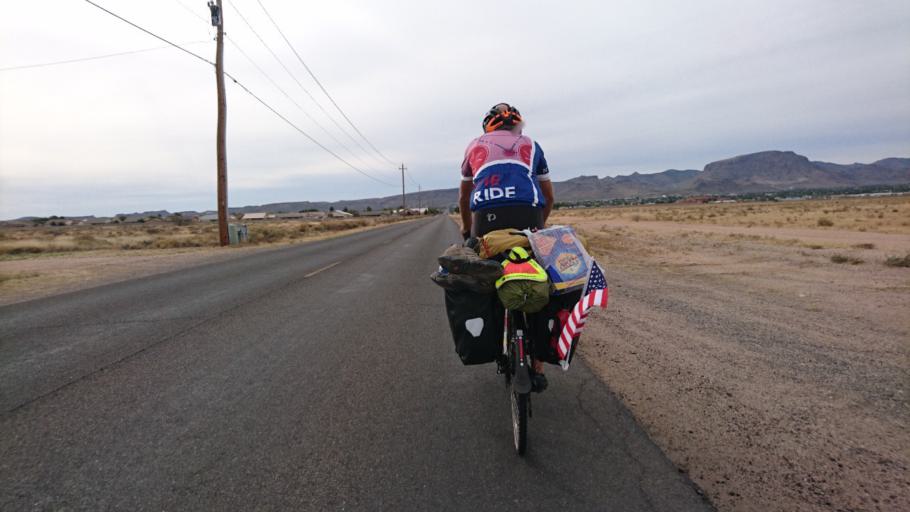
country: US
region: Arizona
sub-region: Mohave County
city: New Kingman-Butler
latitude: 35.2394
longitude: -113.9954
